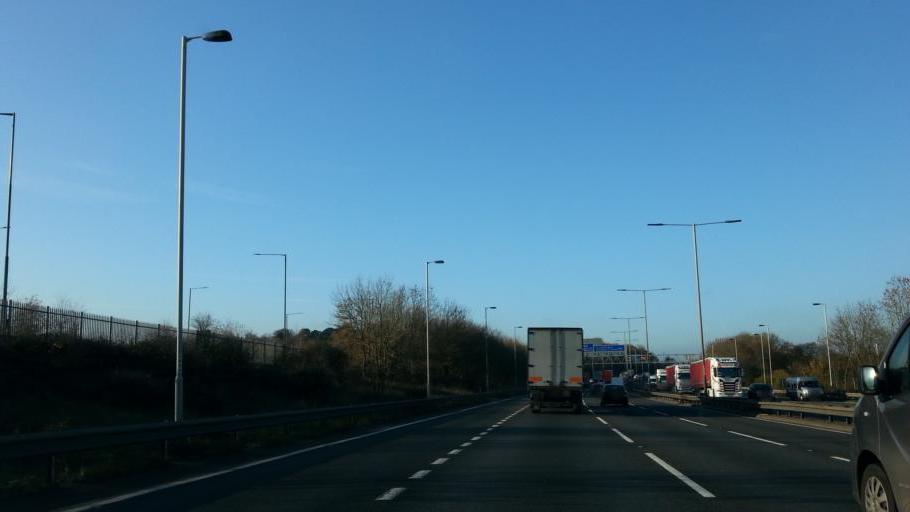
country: GB
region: England
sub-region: Warwickshire
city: Water Orton
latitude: 52.5099
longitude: -1.7817
